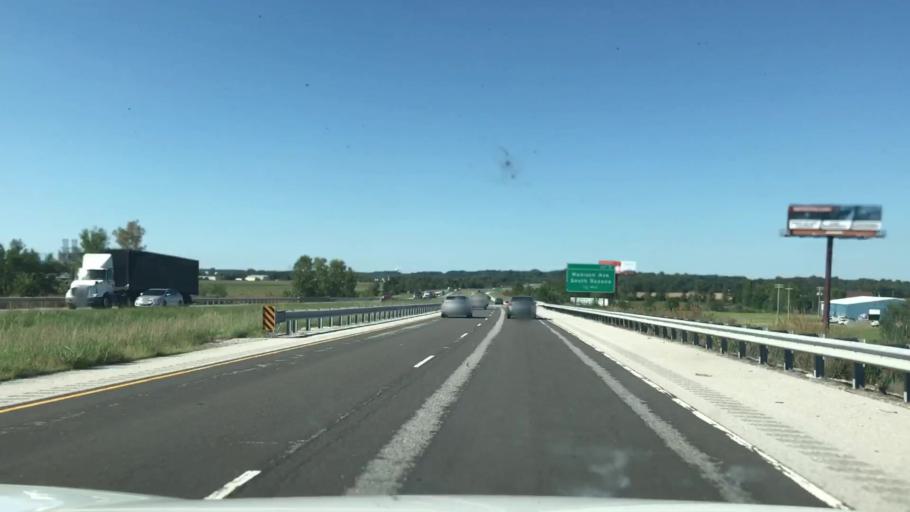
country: US
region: Illinois
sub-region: Madison County
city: South Roxana
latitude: 38.8190
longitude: -90.0420
